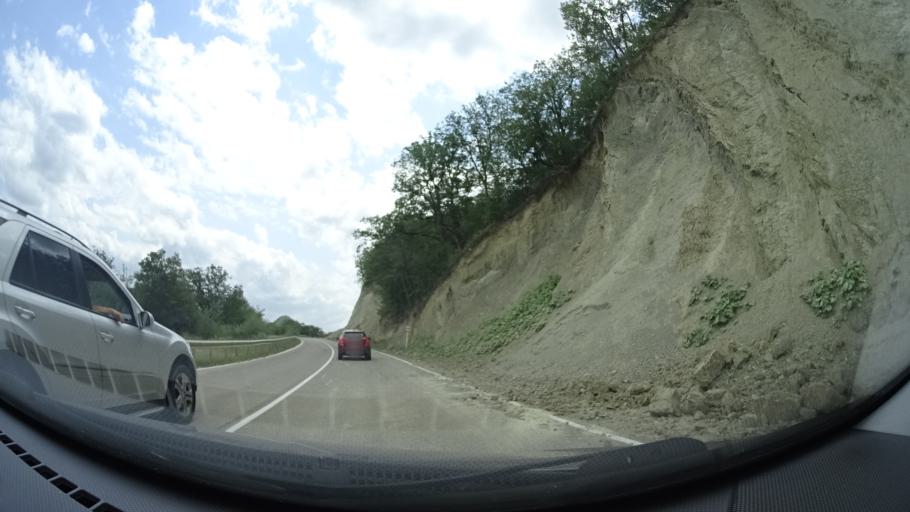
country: GE
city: Didi Lilo
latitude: 41.8171
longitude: 45.1441
